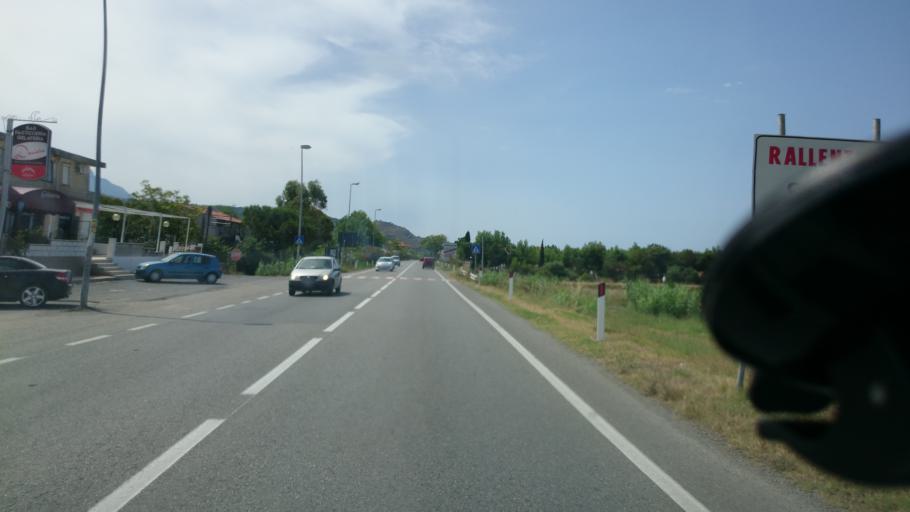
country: IT
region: Calabria
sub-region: Provincia di Cosenza
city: Marcellina
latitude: 39.7453
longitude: 15.8072
